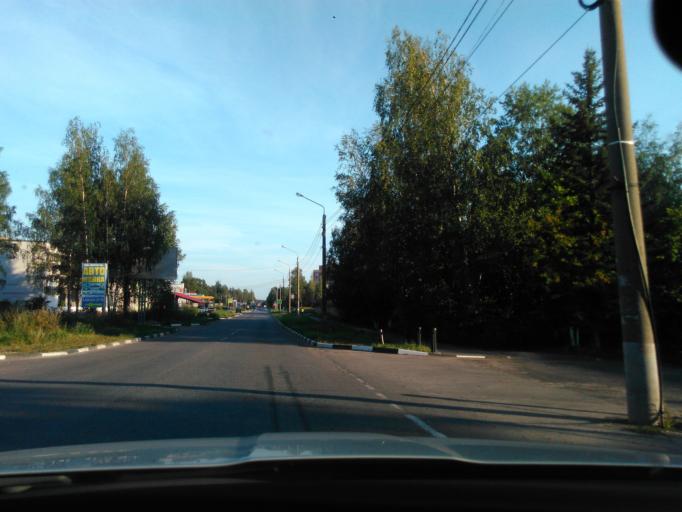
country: RU
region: Tverskaya
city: Konakovo
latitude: 56.7221
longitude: 36.7835
